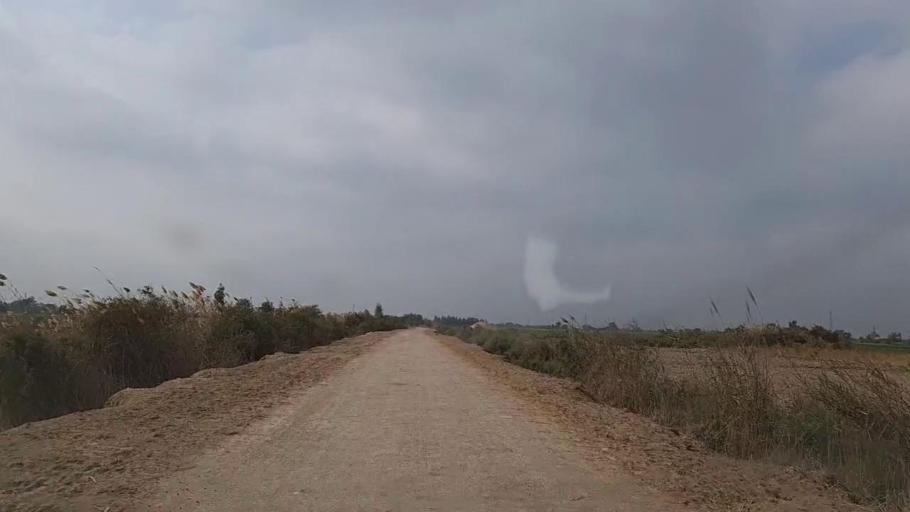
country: PK
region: Sindh
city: Sanghar
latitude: 26.1741
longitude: 68.9598
